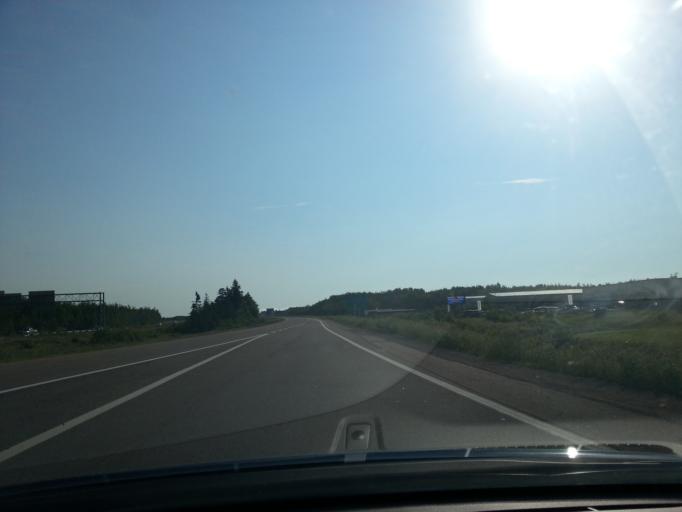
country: CA
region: New Brunswick
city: Dieppe
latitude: 46.1110
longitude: -64.7068
